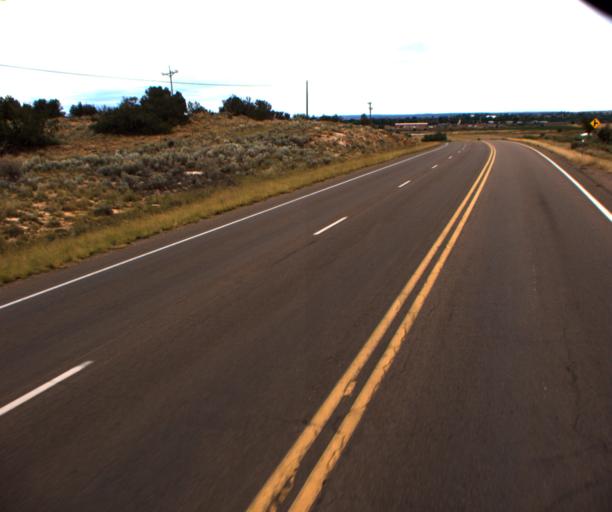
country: US
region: Arizona
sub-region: Navajo County
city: Snowflake
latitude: 34.5323
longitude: -110.0817
